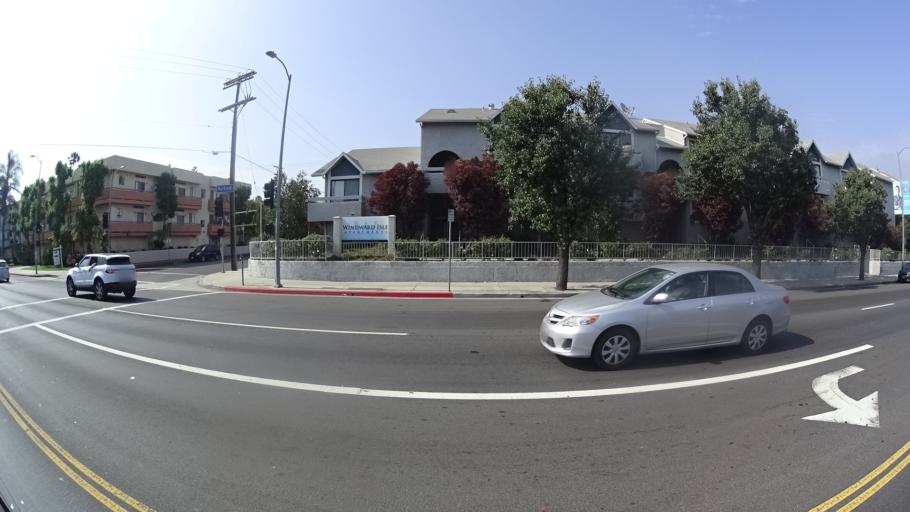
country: US
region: California
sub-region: Los Angeles County
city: Van Nuys
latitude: 34.1722
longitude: -118.4509
